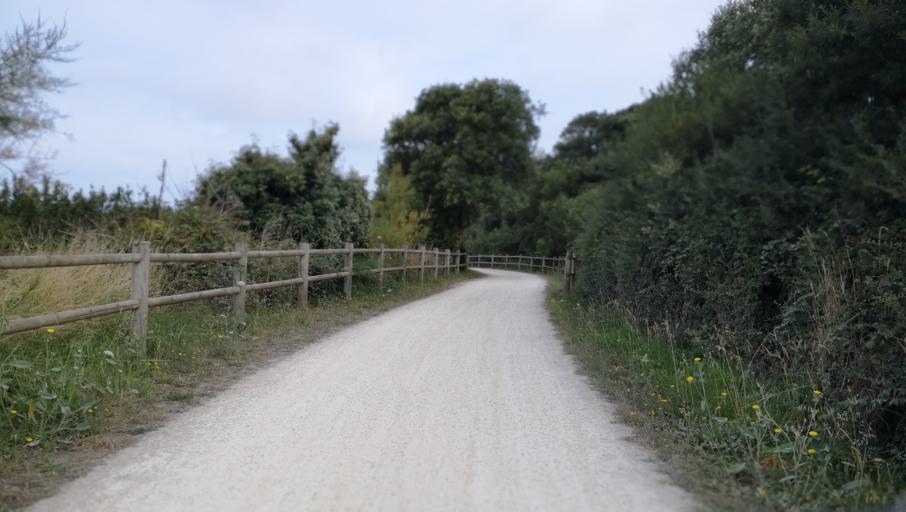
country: FR
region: Pays de la Loire
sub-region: Departement de la Vendee
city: Olonne-sur-Mer
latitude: 46.5282
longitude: -1.8077
